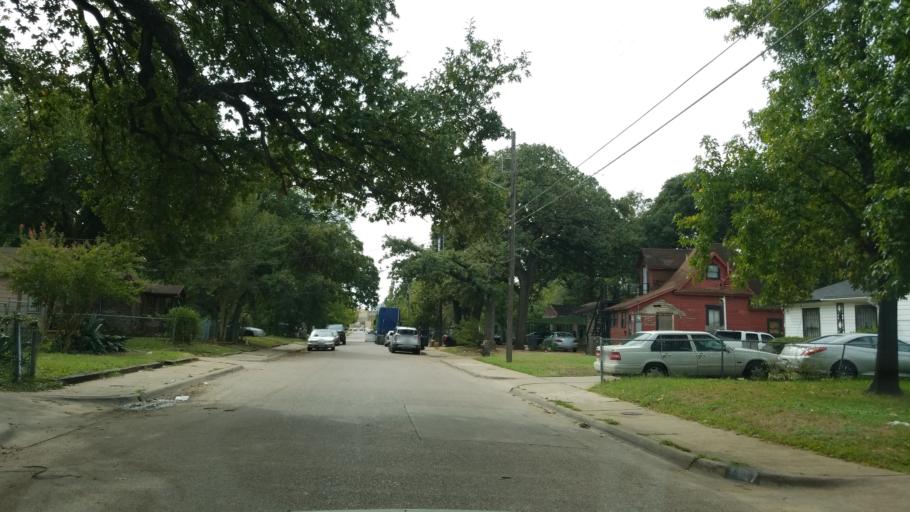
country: US
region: Texas
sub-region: Dallas County
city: Dallas
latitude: 32.7625
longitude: -96.7403
